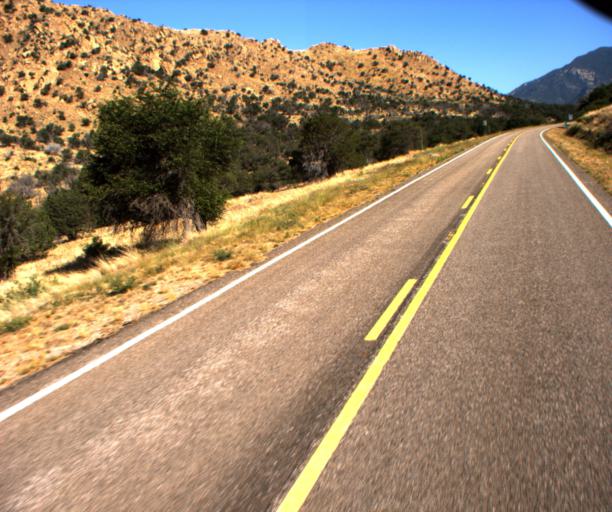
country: US
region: Arizona
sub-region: Graham County
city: Swift Trail Junction
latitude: 32.5837
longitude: -109.8530
